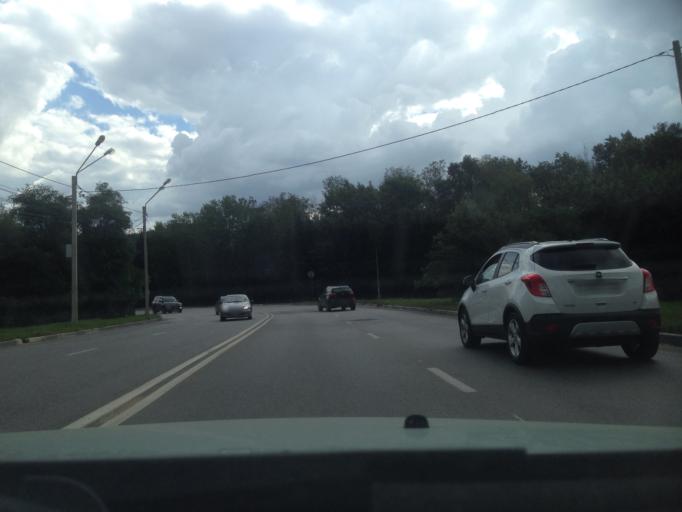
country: RU
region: Voronezj
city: Podgornoye
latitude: 51.7264
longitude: 39.1975
